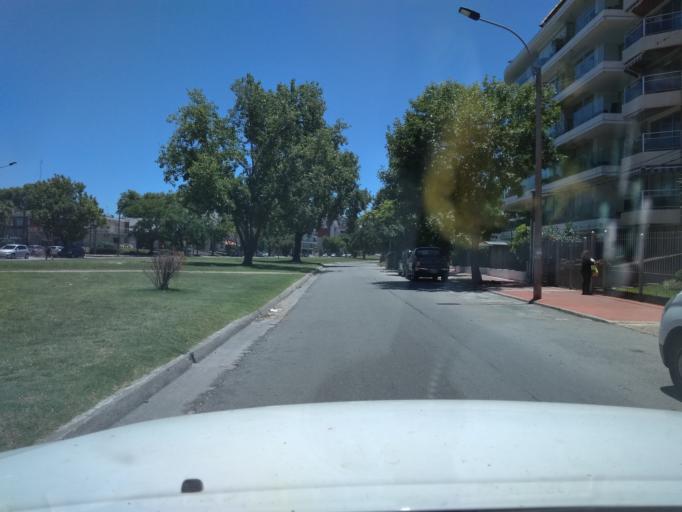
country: UY
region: Canelones
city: Paso de Carrasco
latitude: -34.8943
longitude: -56.1062
